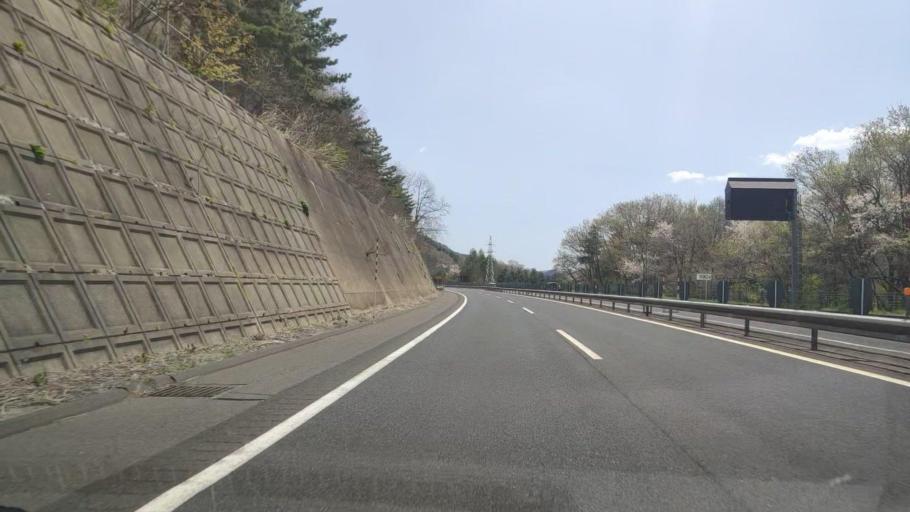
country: JP
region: Iwate
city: Ichinohe
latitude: 40.2317
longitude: 141.3050
